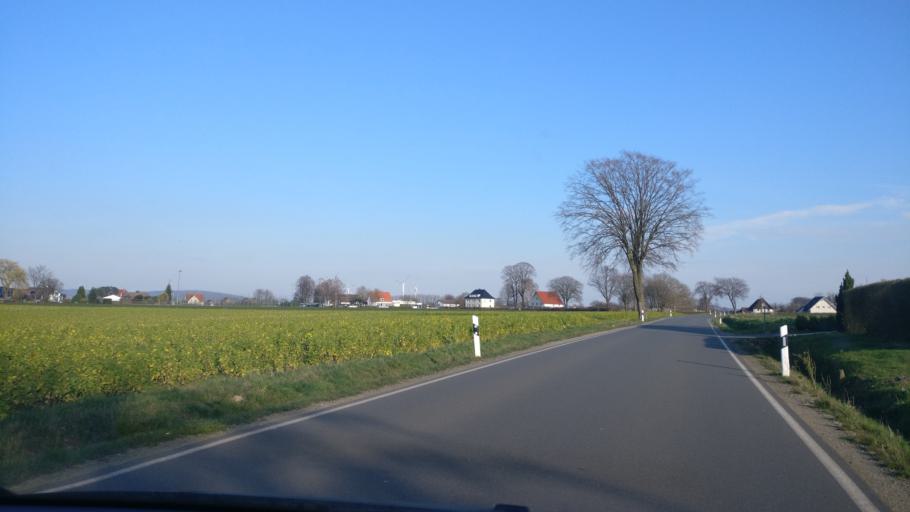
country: DE
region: North Rhine-Westphalia
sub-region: Regierungsbezirk Detmold
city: Lage
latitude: 52.0164
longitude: 8.7794
